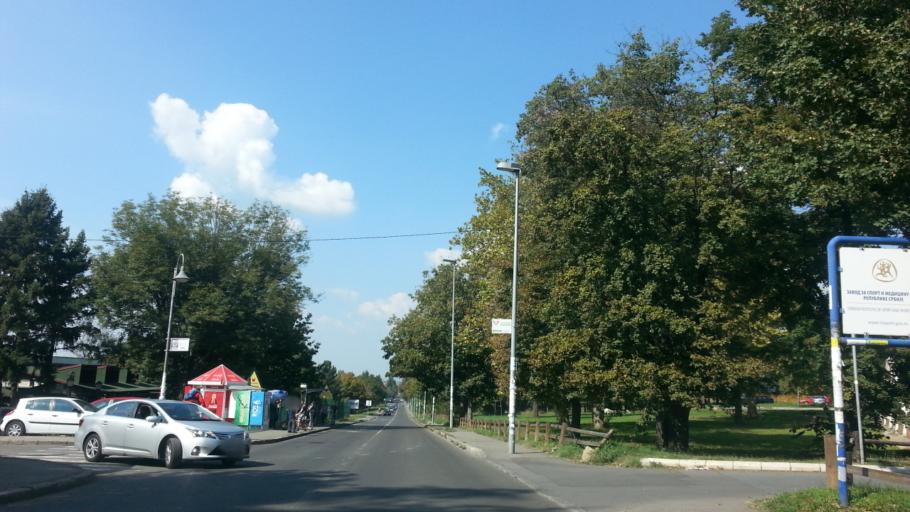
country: RS
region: Central Serbia
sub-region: Belgrade
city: Cukarica
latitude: 44.7641
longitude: 20.4286
